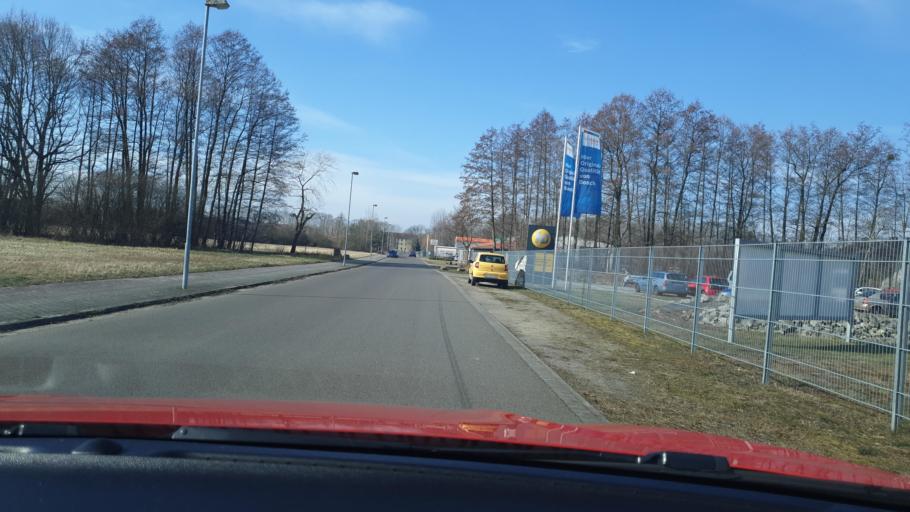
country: DE
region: Saxony
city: Ossling
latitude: 51.4453
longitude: 14.1401
